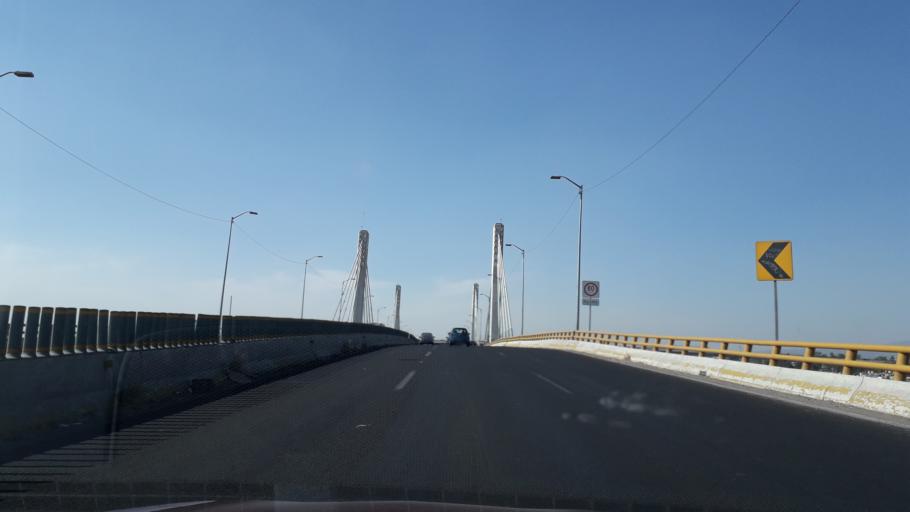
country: MX
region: Puebla
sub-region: Puebla
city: San Sebastian de Aparicio
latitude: 19.0787
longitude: -98.1892
